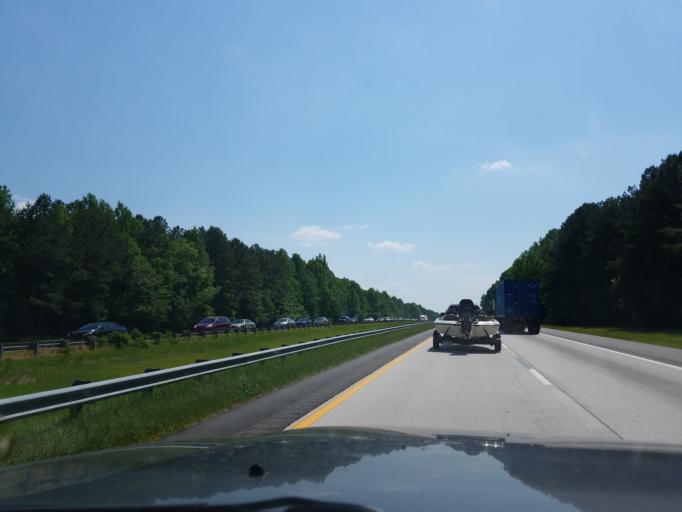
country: US
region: North Carolina
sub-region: Granville County
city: Creedmoor
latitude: 36.2229
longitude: -78.6578
